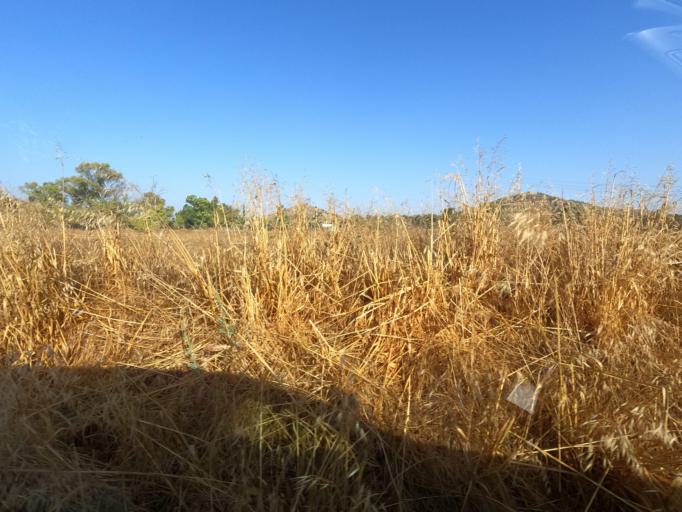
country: CY
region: Lefkosia
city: Lympia
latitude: 34.9815
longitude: 33.4379
